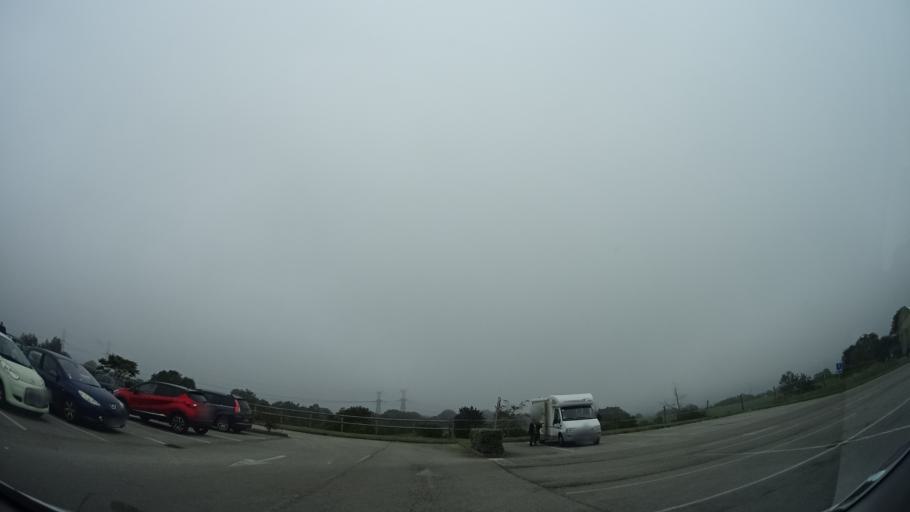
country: FR
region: Lower Normandy
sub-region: Departement de la Manche
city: Les Pieux
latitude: 49.5173
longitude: -1.7983
